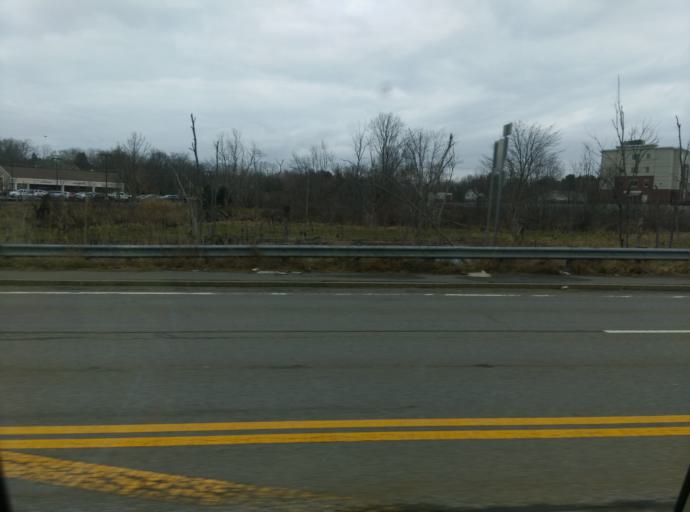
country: US
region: Massachusetts
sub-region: Essex County
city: Amesbury
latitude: 42.8463
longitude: -70.9095
